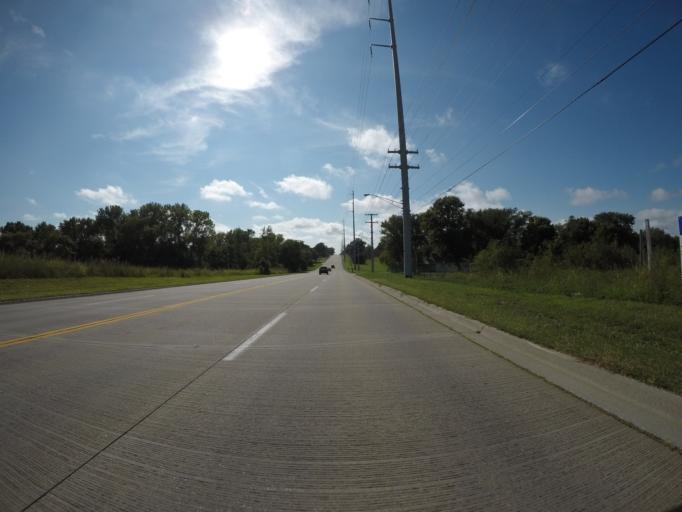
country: US
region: Kansas
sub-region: Wyandotte County
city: Edwardsville
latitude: 39.1287
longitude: -94.8508
